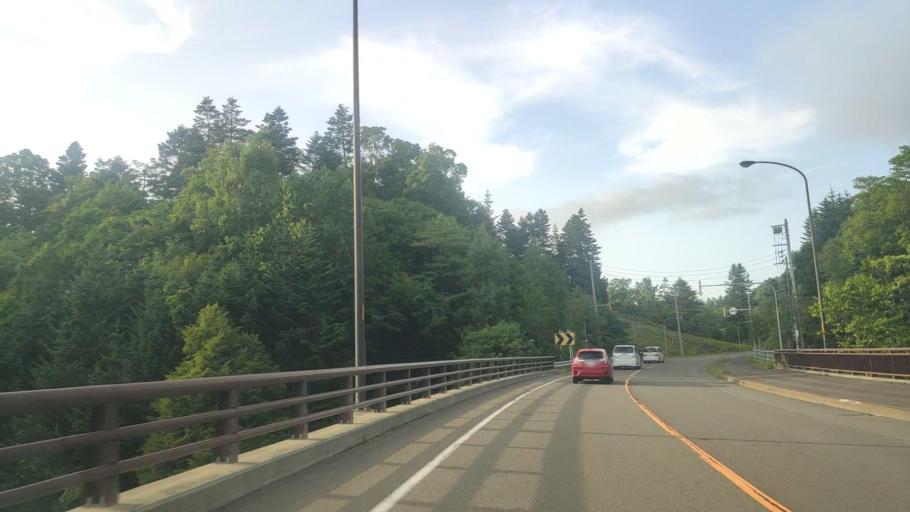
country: JP
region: Hokkaido
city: Iwamizawa
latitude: 43.0258
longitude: 141.9538
